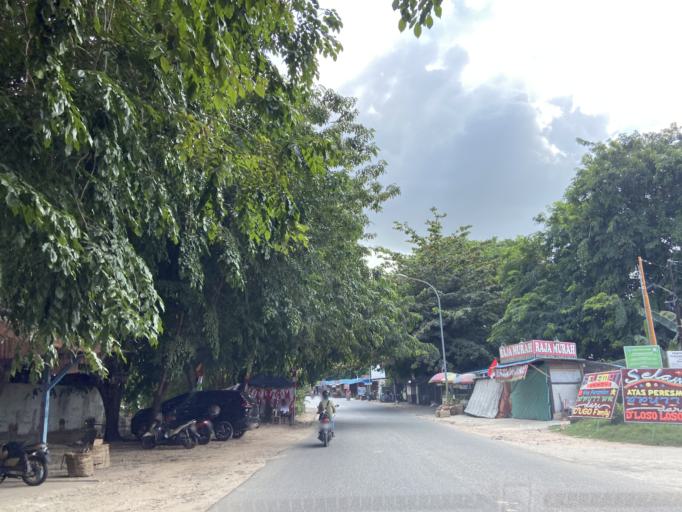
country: SG
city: Singapore
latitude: 1.1337
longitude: 104.0341
